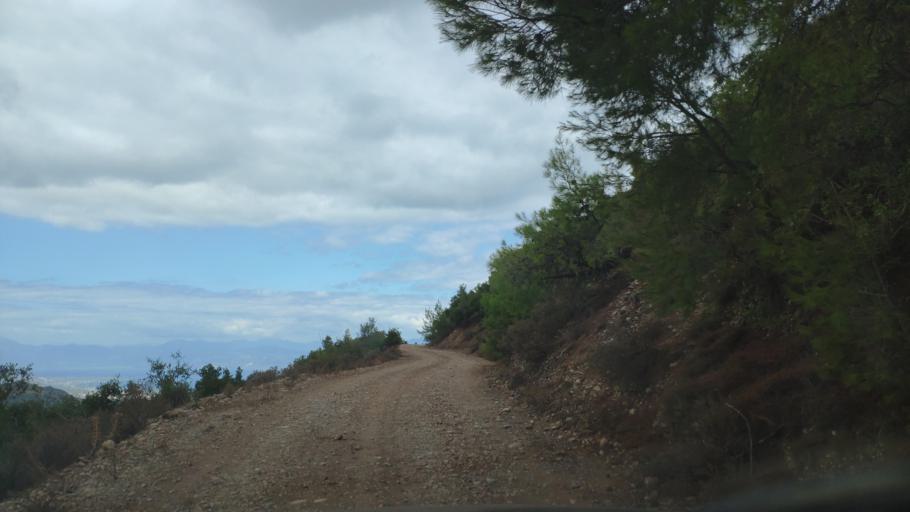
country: GR
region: West Greece
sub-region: Nomos Achaias
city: Temeni
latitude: 38.1719
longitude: 22.1552
